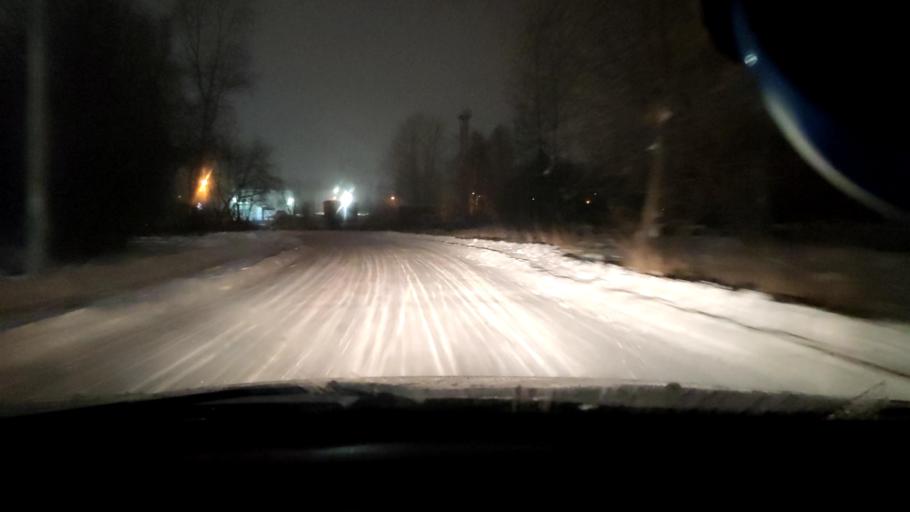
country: RU
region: Perm
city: Overyata
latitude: 58.0089
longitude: 55.9416
